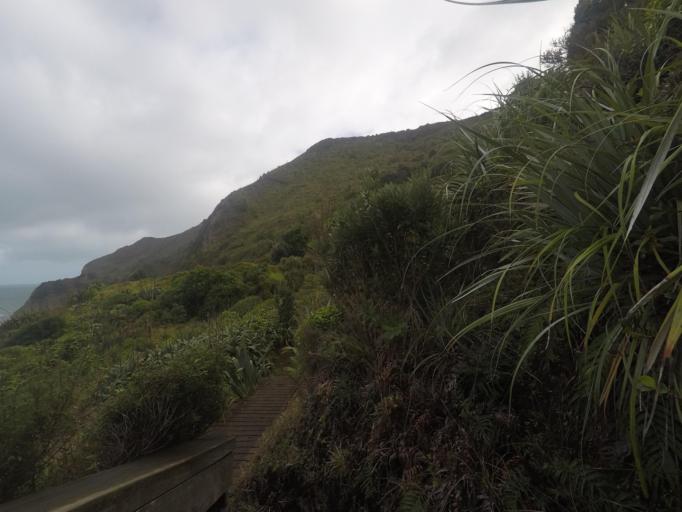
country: NZ
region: Auckland
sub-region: Auckland
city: Muriwai Beach
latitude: -36.8806
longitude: 174.4384
